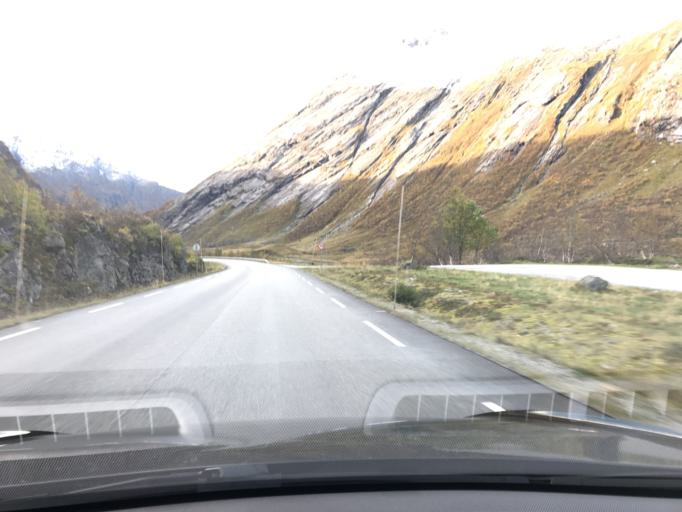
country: NO
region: More og Romsdal
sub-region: Norddal
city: Valldal
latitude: 61.9637
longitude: 7.2537
